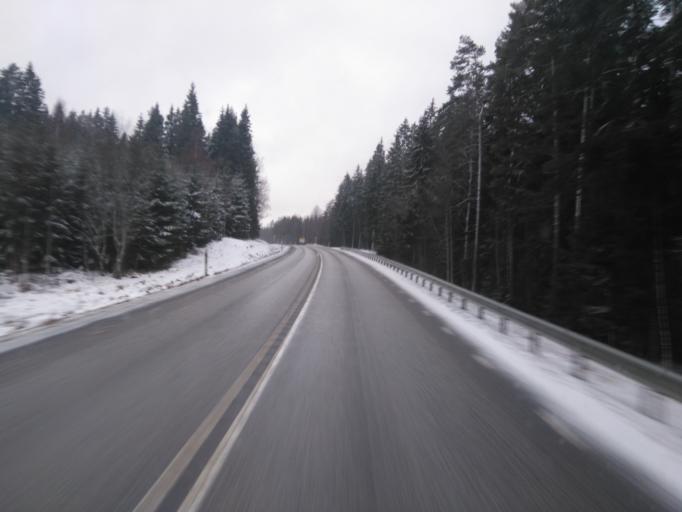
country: SE
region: Joenkoeping
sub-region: Eksjo Kommun
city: Eksjoe
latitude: 57.6504
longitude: 15.0472
